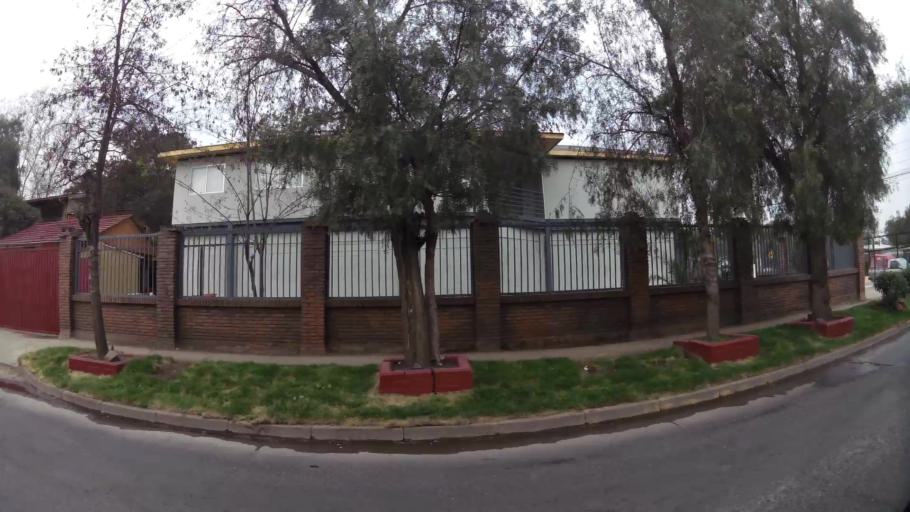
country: CL
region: Santiago Metropolitan
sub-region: Provincia de Chacabuco
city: Chicureo Abajo
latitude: -33.1952
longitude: -70.6752
